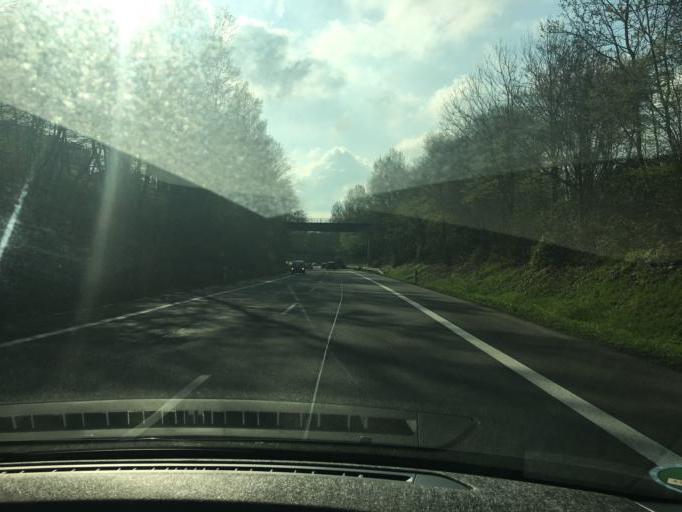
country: DE
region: North Rhine-Westphalia
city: Bornheim
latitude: 50.7242
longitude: 6.9180
